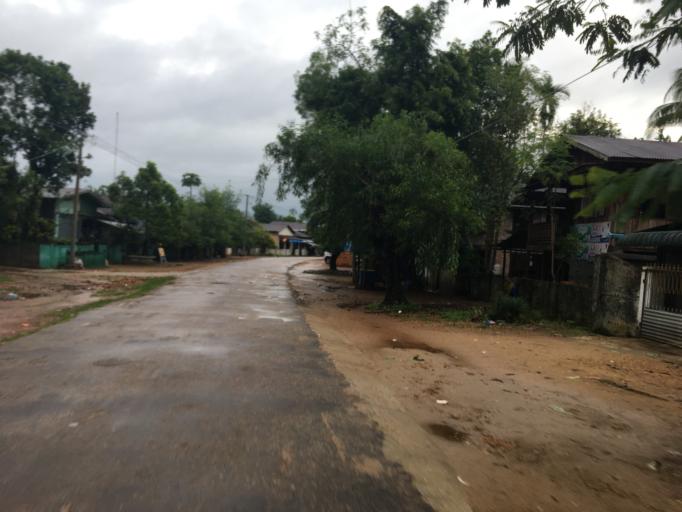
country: MM
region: Mon
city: Mudon
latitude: 16.0386
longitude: 98.1187
